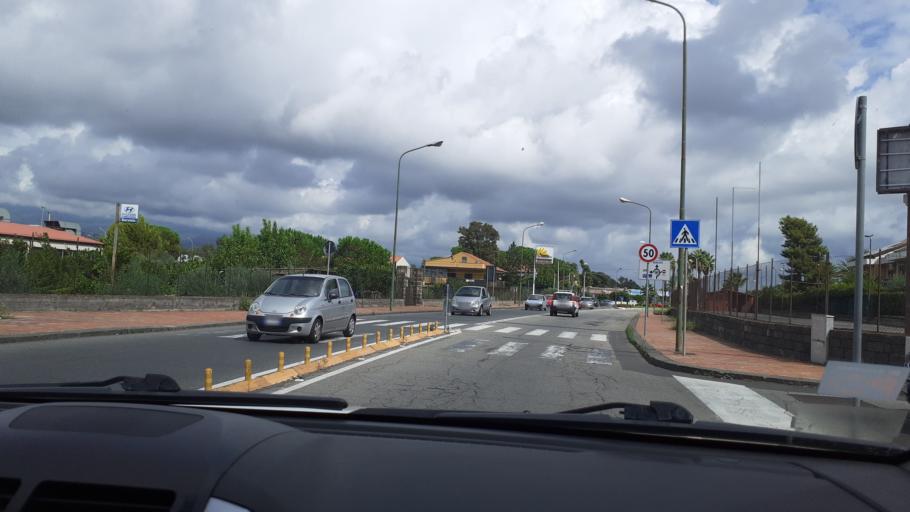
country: IT
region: Sicily
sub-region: Catania
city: San Gregorio di Catania
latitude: 37.5662
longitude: 15.1057
